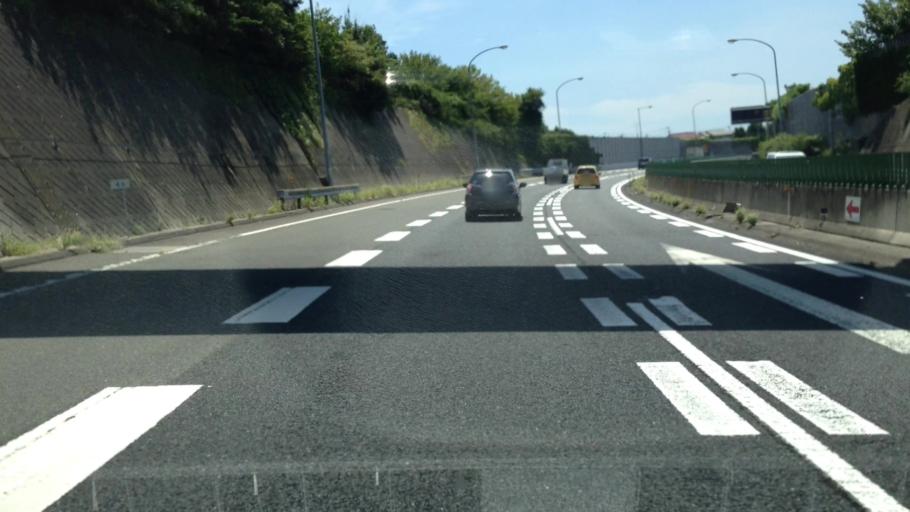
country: JP
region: Kanagawa
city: Yokohama
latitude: 35.4151
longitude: 139.5807
